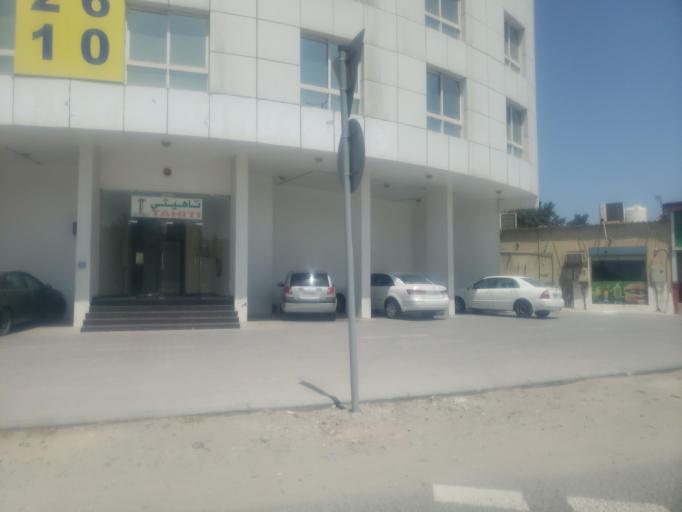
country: AE
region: Ra's al Khaymah
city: Ras al-Khaimah
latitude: 25.8055
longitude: 55.9615
